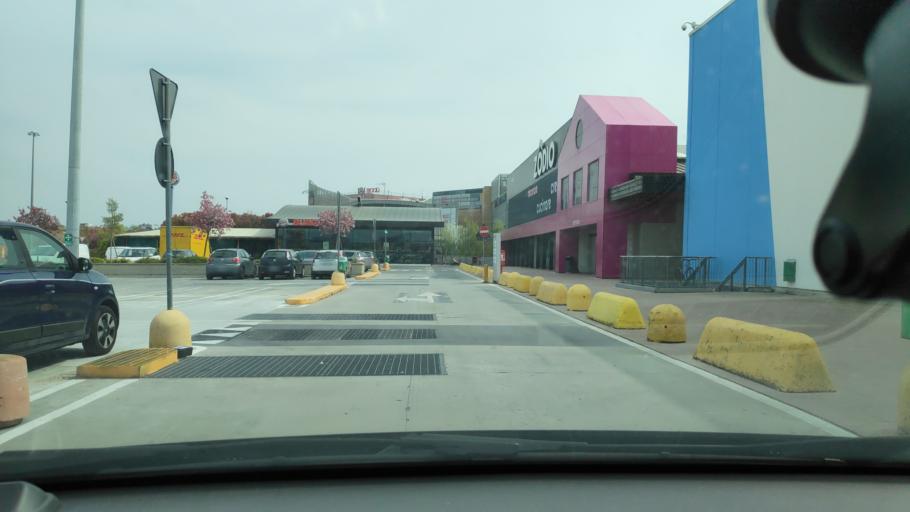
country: IT
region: Lombardy
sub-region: Citta metropolitana di Milano
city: Rozzano
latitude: 45.3897
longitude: 9.1758
